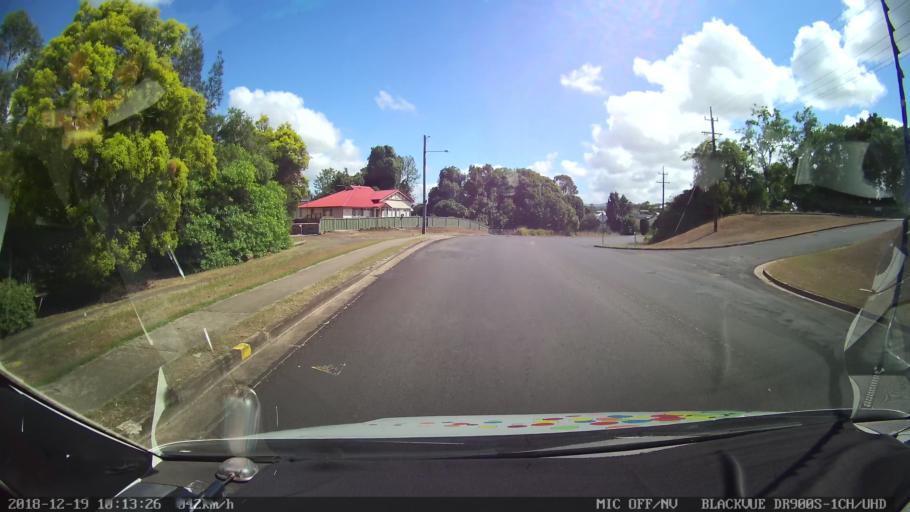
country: AU
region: New South Wales
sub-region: Kyogle
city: Kyogle
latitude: -28.6174
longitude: 153.0043
